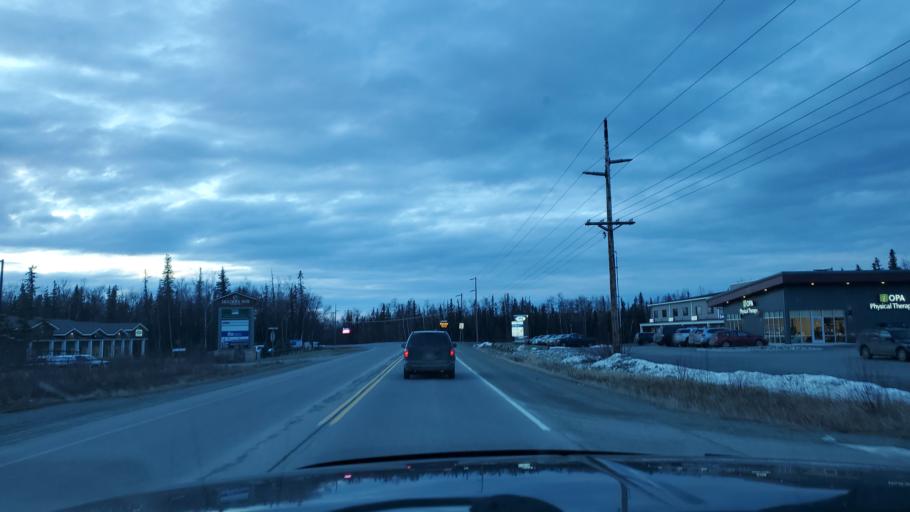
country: US
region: Alaska
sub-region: Matanuska-Susitna Borough
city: Wasilla
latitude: 61.5889
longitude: -149.4105
